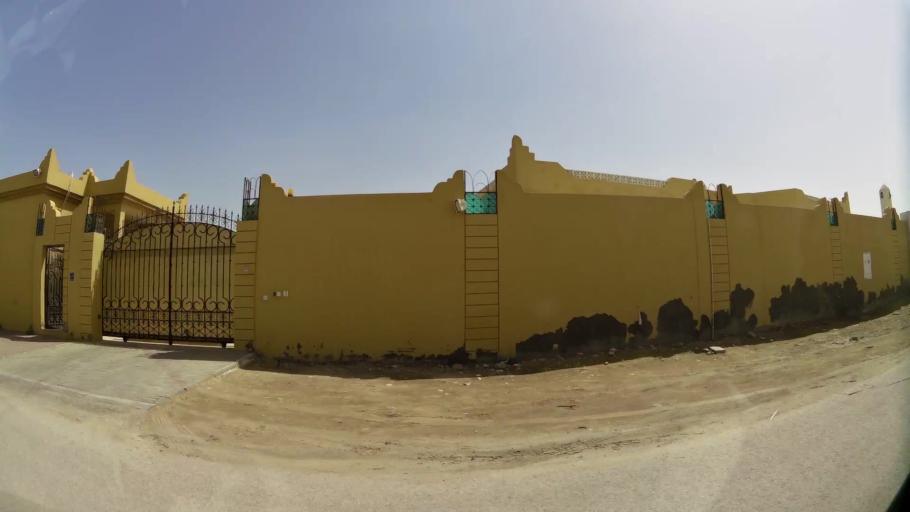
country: QA
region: Baladiyat Umm Salal
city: Umm Salal Muhammad
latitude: 25.3808
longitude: 51.4258
